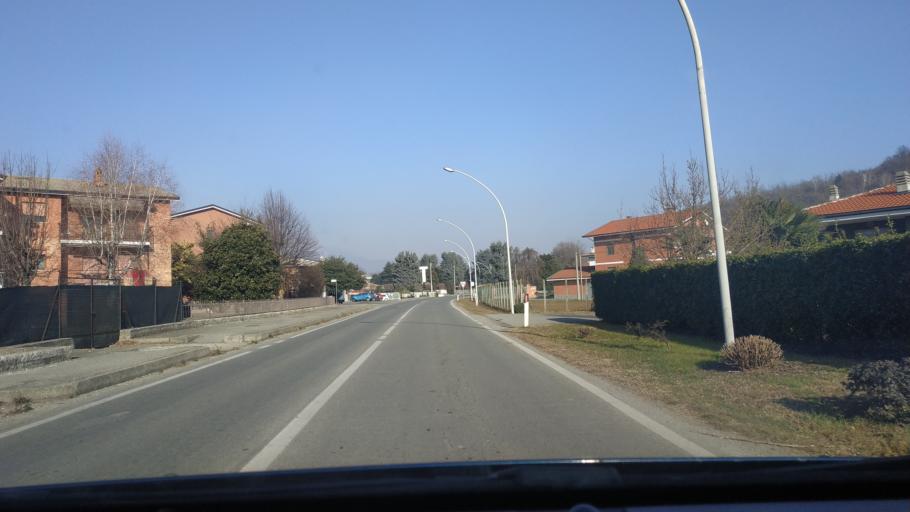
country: IT
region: Piedmont
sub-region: Provincia di Torino
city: Pavone Canavese
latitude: 45.4419
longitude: 7.8525
